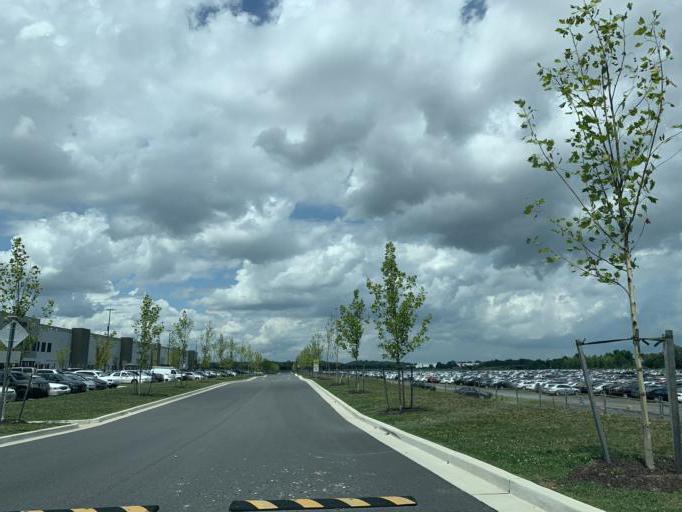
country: US
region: Maryland
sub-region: Baltimore County
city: Edgemere
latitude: 39.2290
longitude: -76.4681
